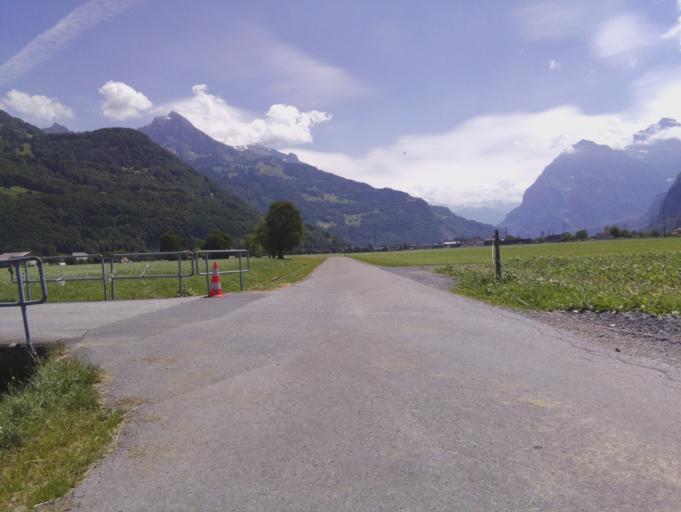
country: CH
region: Glarus
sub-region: Glarus
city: Oberurnen
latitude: 47.1180
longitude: 9.0671
